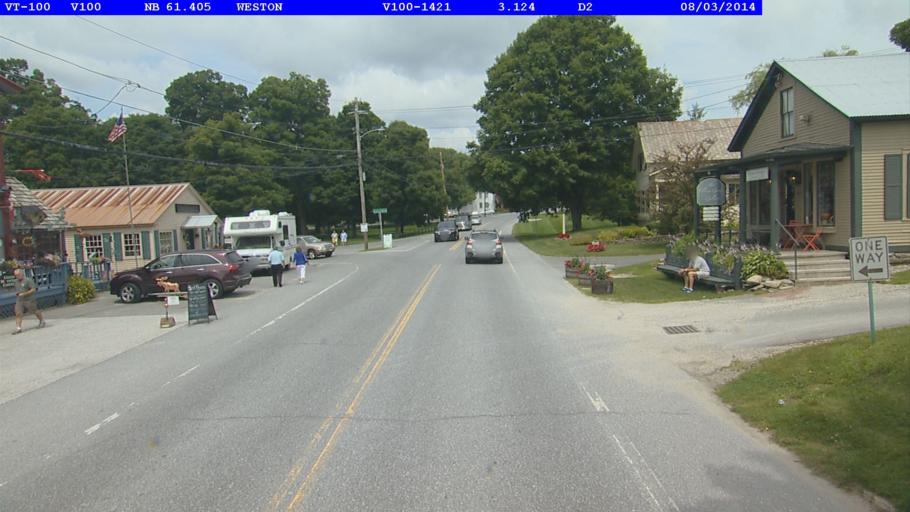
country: US
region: Vermont
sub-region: Windsor County
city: Chester
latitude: 43.2908
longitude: -72.7929
